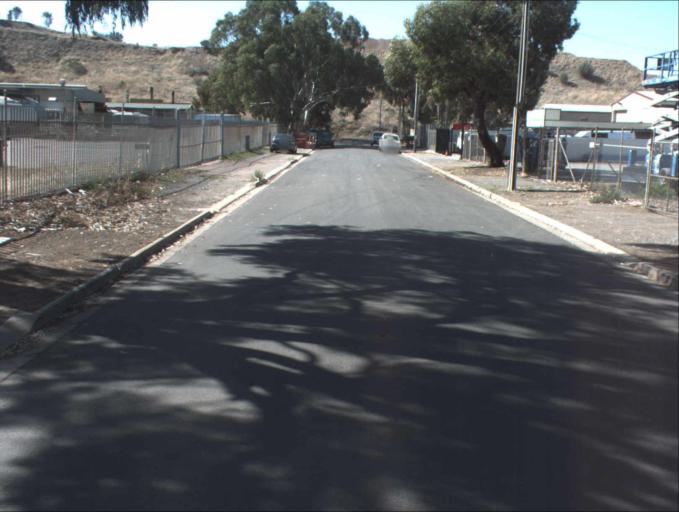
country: AU
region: South Australia
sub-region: Charles Sturt
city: Woodville North
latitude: -34.8360
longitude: 138.5577
